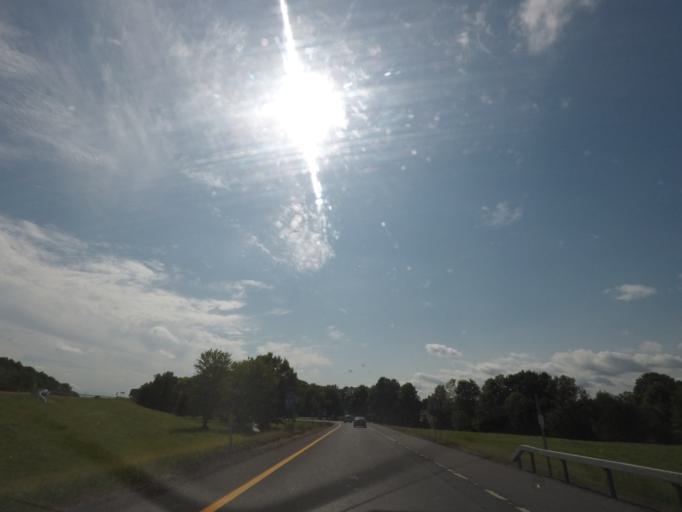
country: US
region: New York
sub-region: Rensselaer County
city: East Greenbush
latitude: 42.5817
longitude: -73.6794
